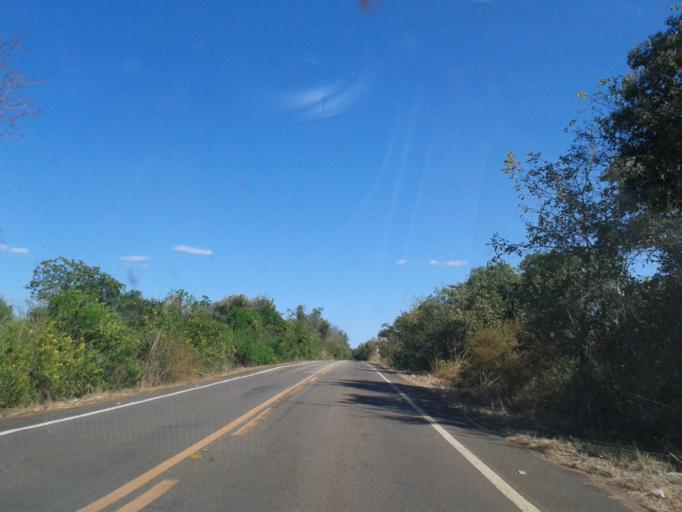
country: BR
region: Goias
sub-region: Crixas
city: Crixas
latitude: -14.0051
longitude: -50.3251
